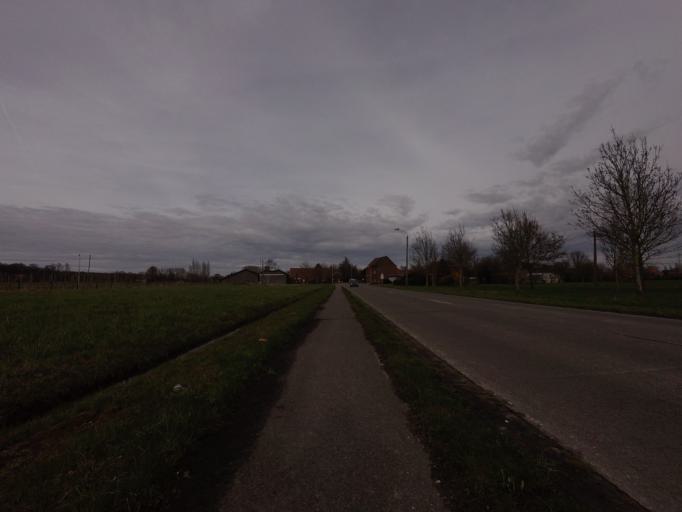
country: BE
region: Flanders
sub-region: Provincie Antwerpen
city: Lint
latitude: 51.1306
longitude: 4.5294
